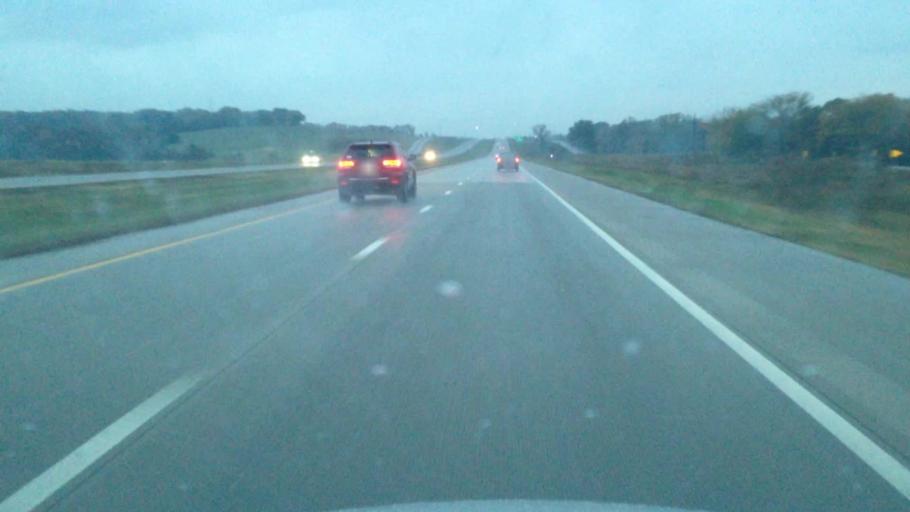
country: US
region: Kansas
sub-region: Douglas County
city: Baldwin City
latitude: 38.8028
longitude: -95.2692
